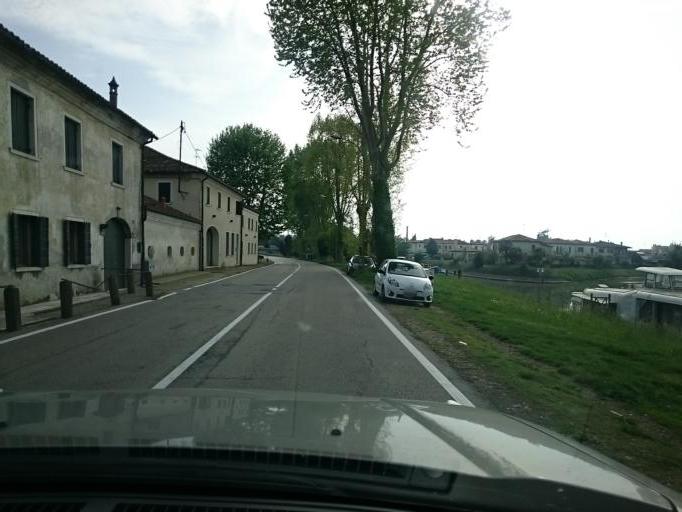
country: IT
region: Veneto
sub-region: Provincia di Venezia
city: Mira Taglio
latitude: 45.4375
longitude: 12.1428
